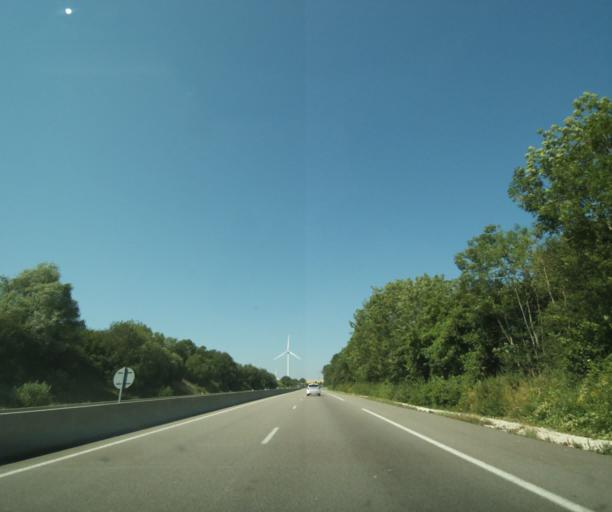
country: FR
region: Lorraine
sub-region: Departement de la Meuse
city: Ligny-en-Barrois
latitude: 48.7044
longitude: 5.4459
